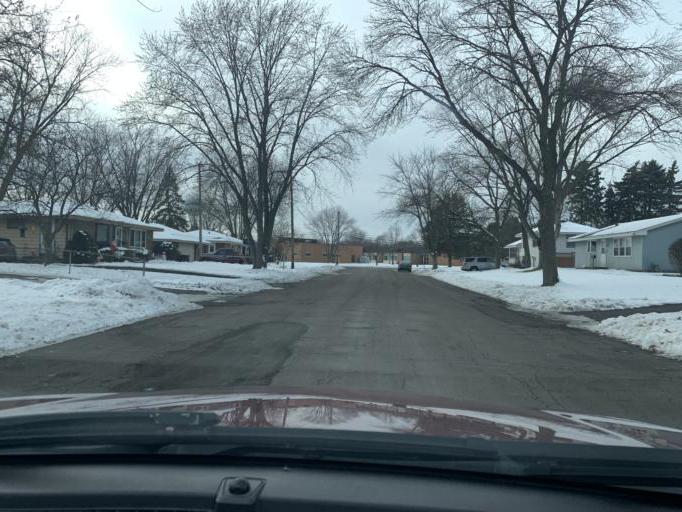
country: US
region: Minnesota
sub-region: Washington County
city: Saint Paul Park
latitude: 44.8357
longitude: -92.9786
